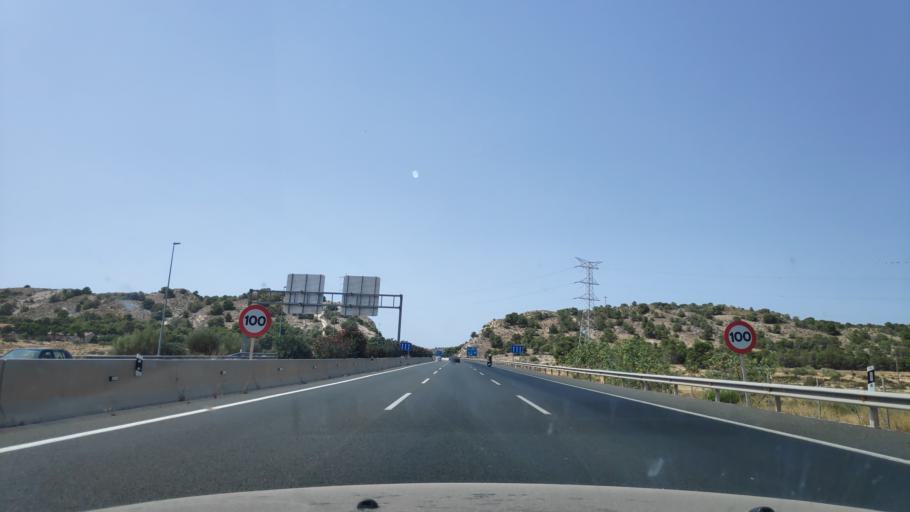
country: ES
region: Murcia
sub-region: Murcia
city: Murcia
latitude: 37.8694
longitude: -1.1240
